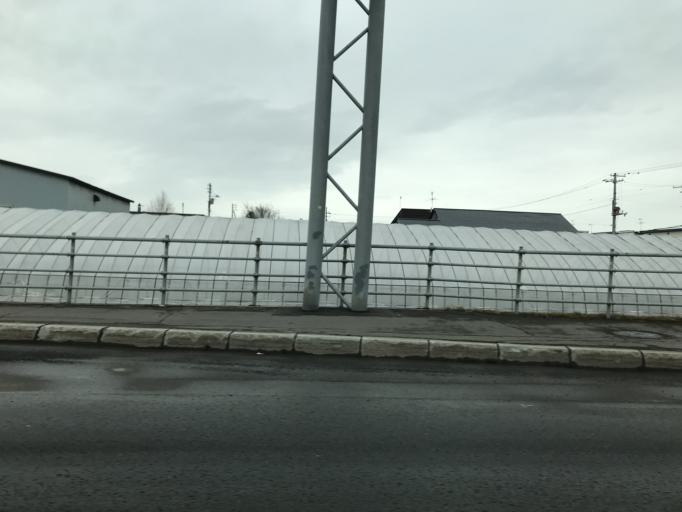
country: JP
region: Hokkaido
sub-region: Asahikawa-shi
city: Asahikawa
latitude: 43.8260
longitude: 142.4177
